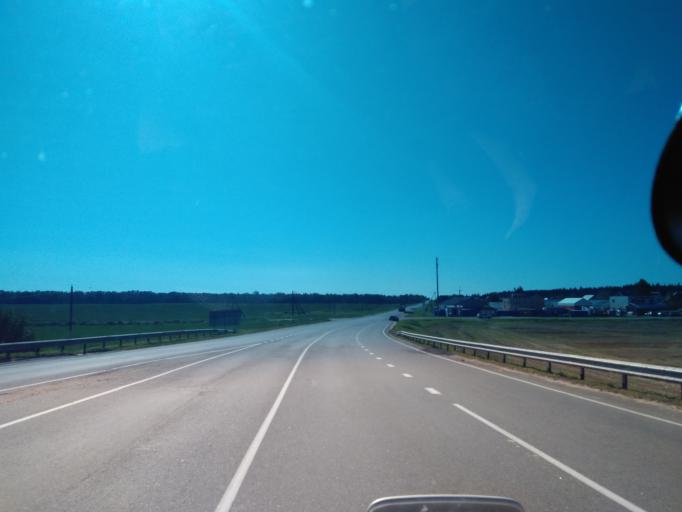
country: BY
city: Fanipol
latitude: 53.7667
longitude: 27.3500
